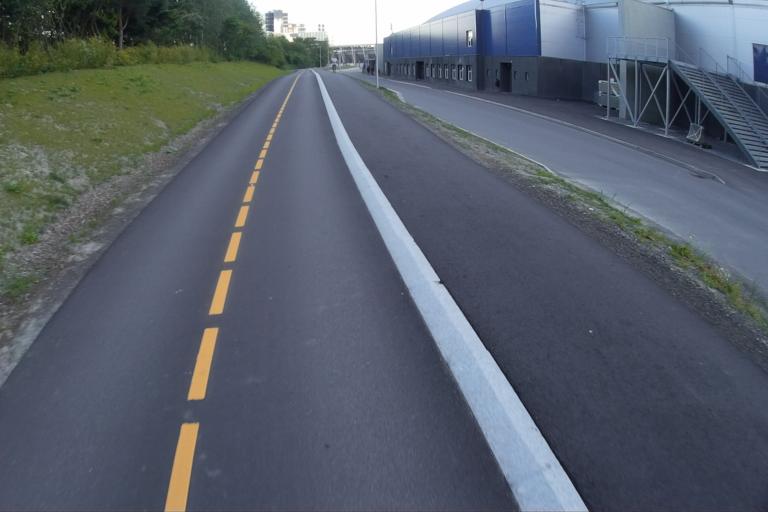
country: NO
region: Oslo
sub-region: Oslo
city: Oslo
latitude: 59.9211
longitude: 10.8065
